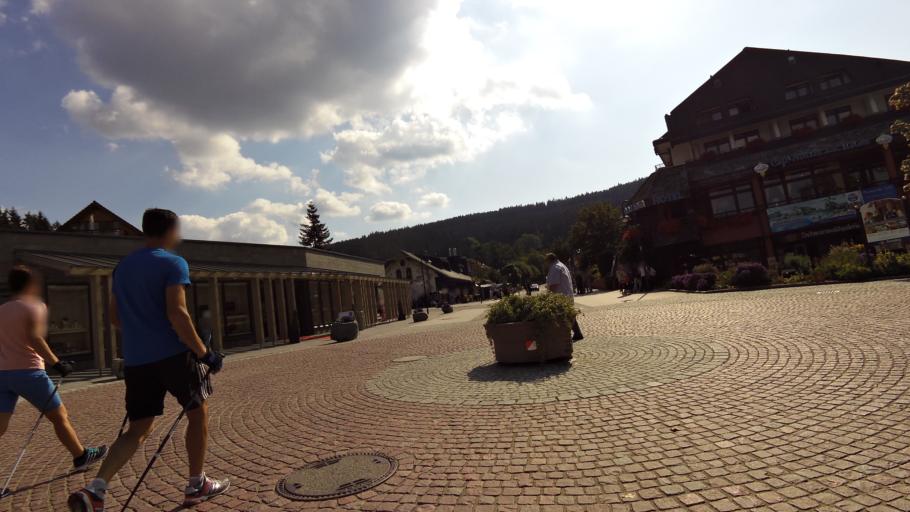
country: DE
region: Baden-Wuerttemberg
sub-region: Freiburg Region
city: Titisee-Neustadt
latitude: 47.8988
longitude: 8.1544
